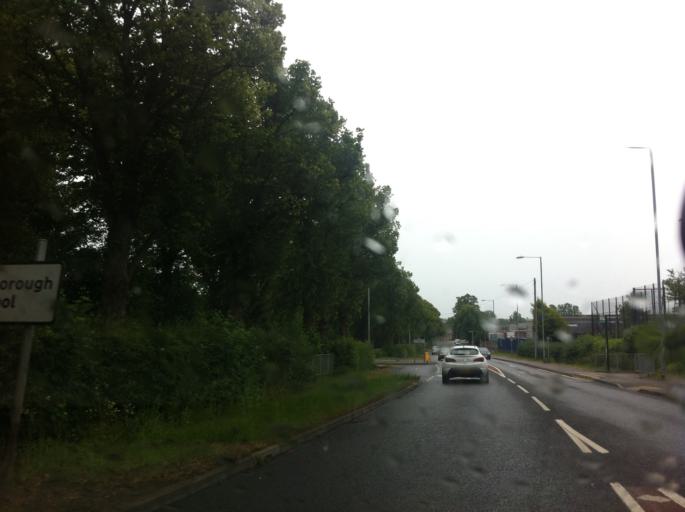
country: GB
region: England
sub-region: Northamptonshire
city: Wellingborough
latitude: 52.2968
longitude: -0.6876
